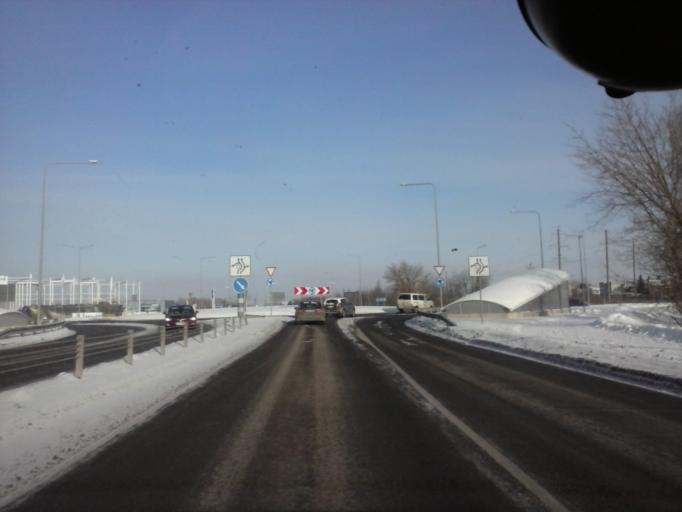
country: EE
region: Tartu
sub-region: Tartu linn
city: Tartu
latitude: 58.3665
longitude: 26.6783
